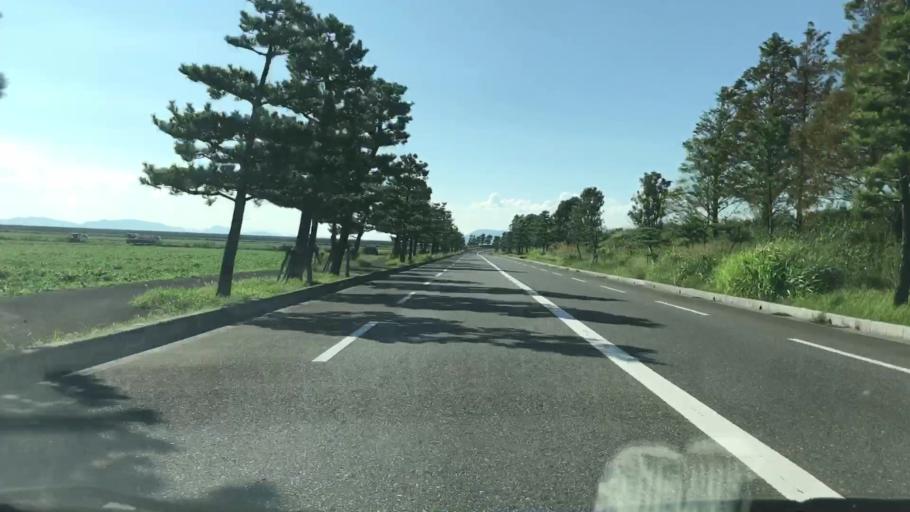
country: JP
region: Saga Prefecture
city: Okawa
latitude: 33.1583
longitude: 130.2944
